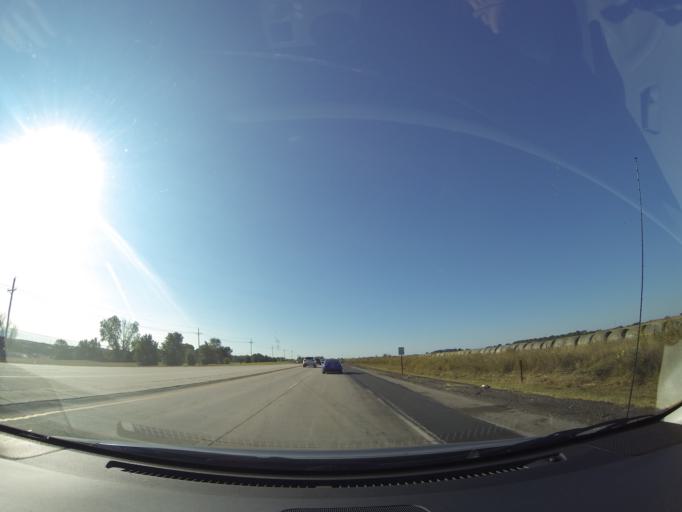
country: US
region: Nebraska
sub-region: Douglas County
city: Elkhorn
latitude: 41.2189
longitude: -96.2344
